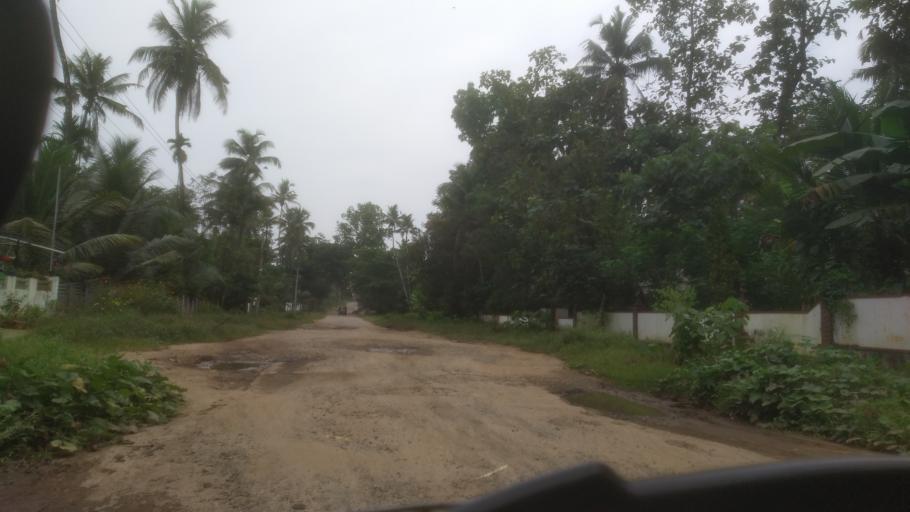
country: IN
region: Kerala
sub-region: Ernakulam
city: Perumbavoor
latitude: 10.0532
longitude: 76.5207
